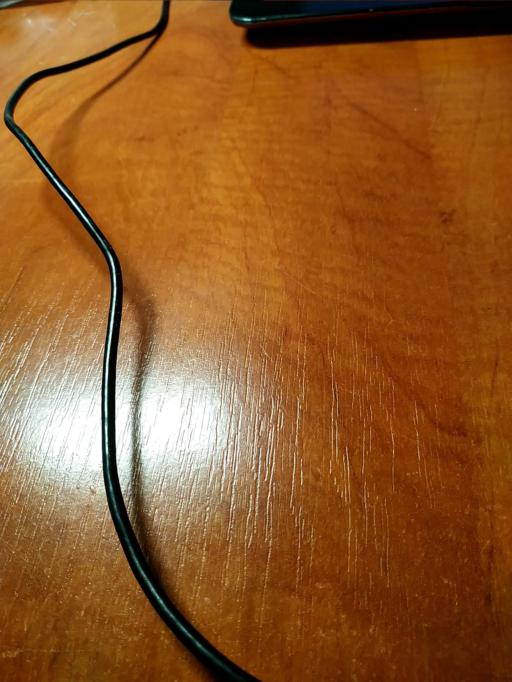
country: BY
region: Mogilev
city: Khotsimsk
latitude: 53.5400
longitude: 32.5008
